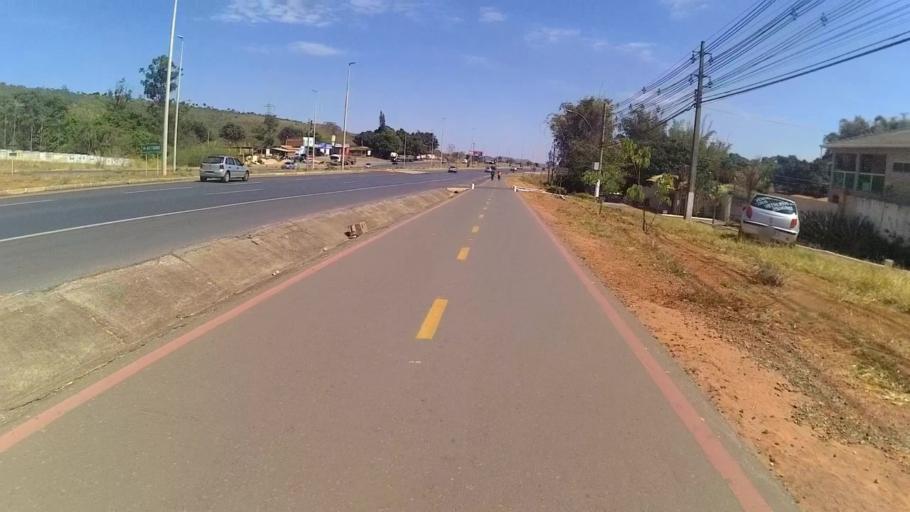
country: BR
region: Federal District
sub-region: Brasilia
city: Brasilia
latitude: -15.6605
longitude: -47.8441
